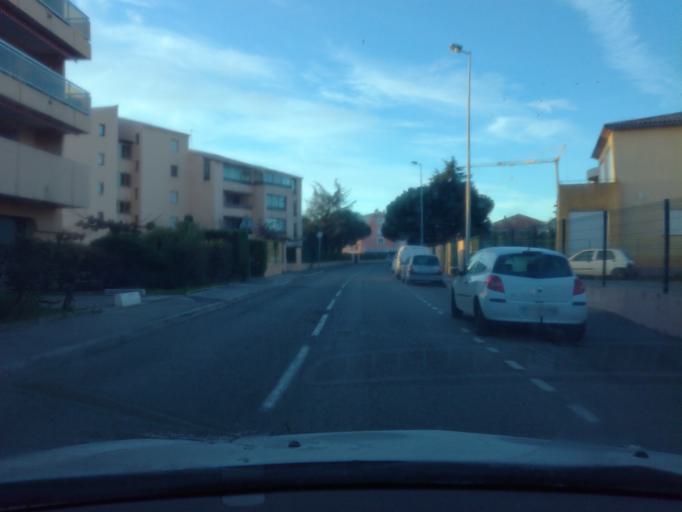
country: FR
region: Provence-Alpes-Cote d'Azur
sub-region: Departement du Var
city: Frejus
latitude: 43.4329
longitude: 6.7458
